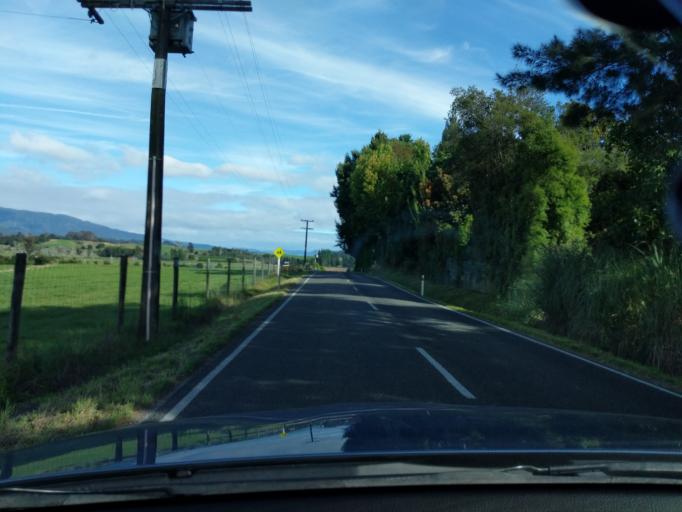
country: NZ
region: Tasman
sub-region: Tasman District
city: Takaka
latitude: -40.8511
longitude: 172.8427
